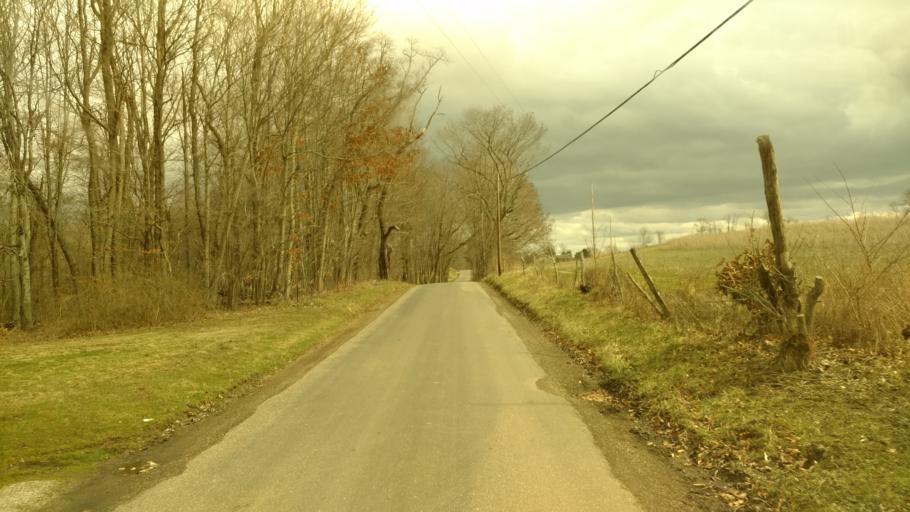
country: US
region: Ohio
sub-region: Muskingum County
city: Frazeysburg
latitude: 40.0611
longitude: -82.0967
